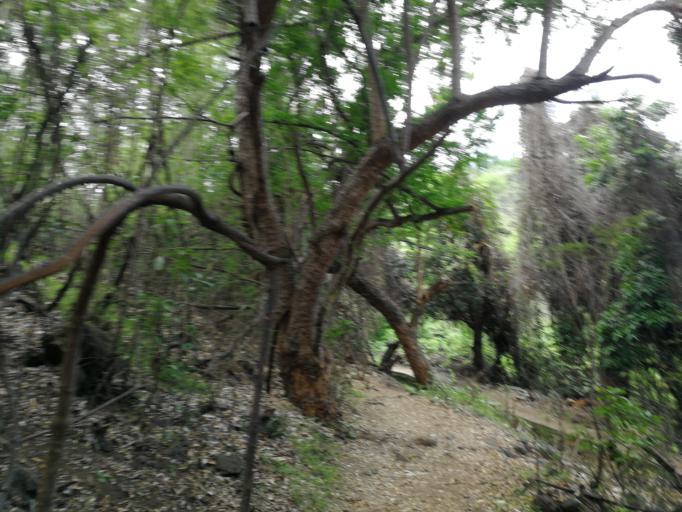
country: RE
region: Reunion
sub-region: Reunion
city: Saint-Paul
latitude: -21.0446
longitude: 55.2433
